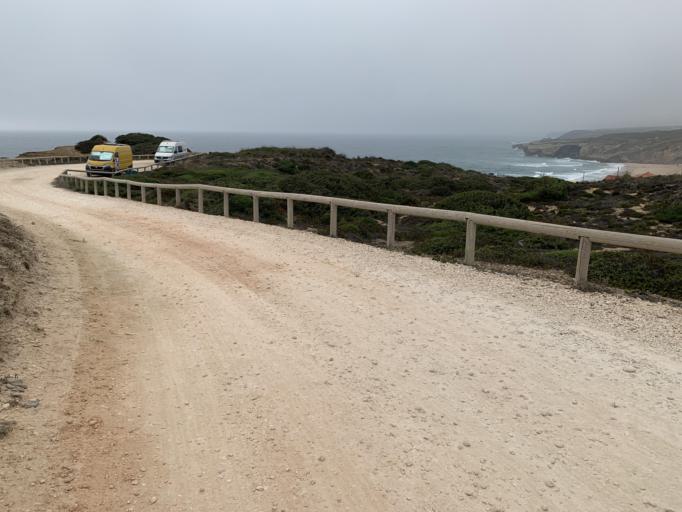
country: PT
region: Faro
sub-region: Aljezur
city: Aljezur
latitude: 37.3386
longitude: -8.8559
